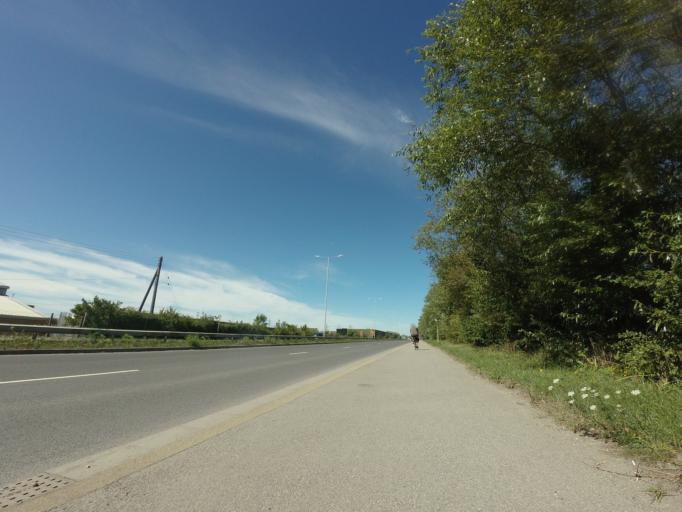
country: GB
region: England
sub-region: Kent
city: Sandwich
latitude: 51.3029
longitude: 1.3473
